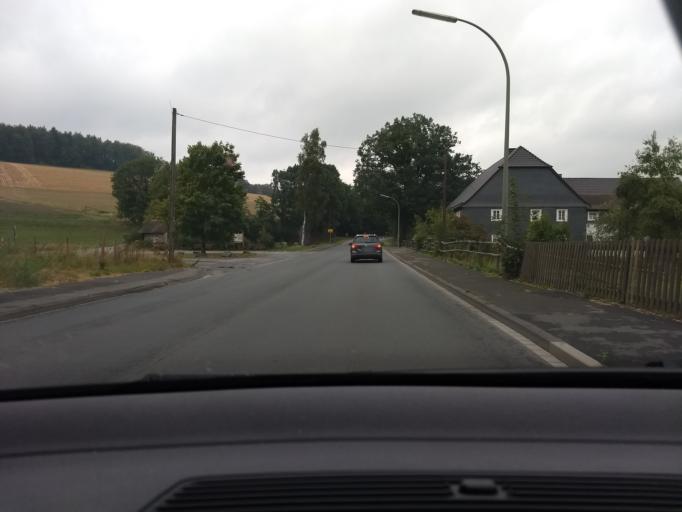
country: DE
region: North Rhine-Westphalia
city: Eslohe
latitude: 51.3410
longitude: 8.1688
